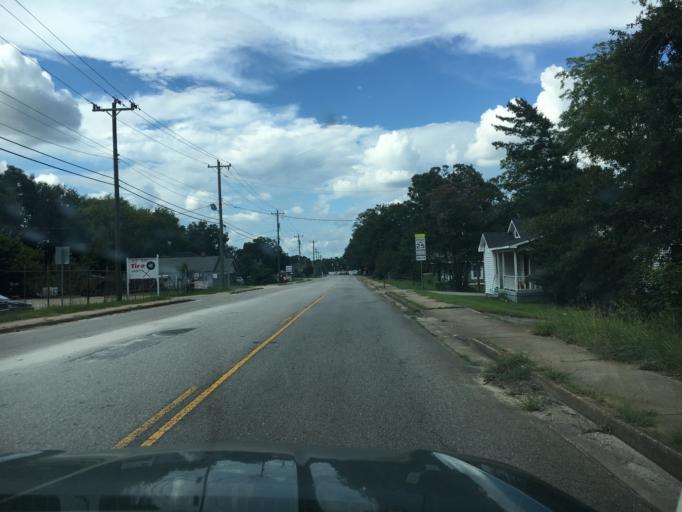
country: US
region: South Carolina
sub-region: Spartanburg County
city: Southern Shops
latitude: 34.9867
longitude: -81.9730
